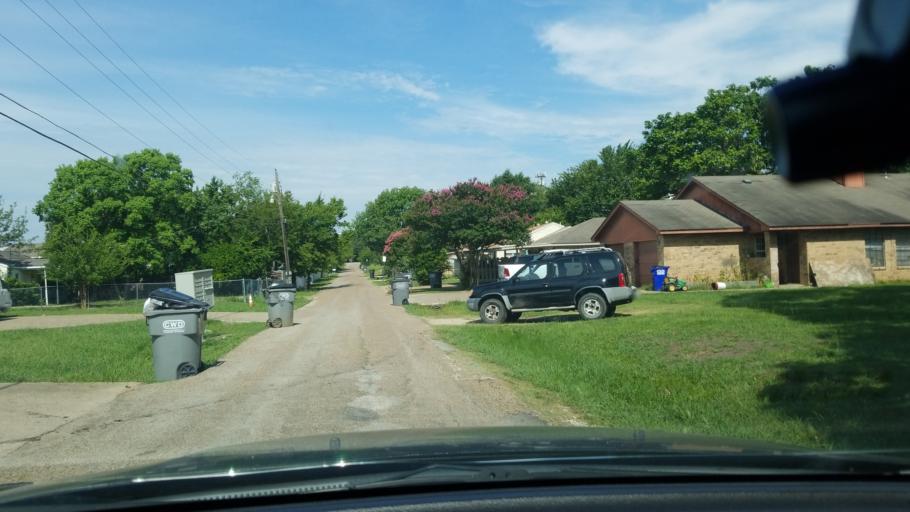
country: US
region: Texas
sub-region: Dallas County
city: Balch Springs
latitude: 32.7301
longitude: -96.6286
